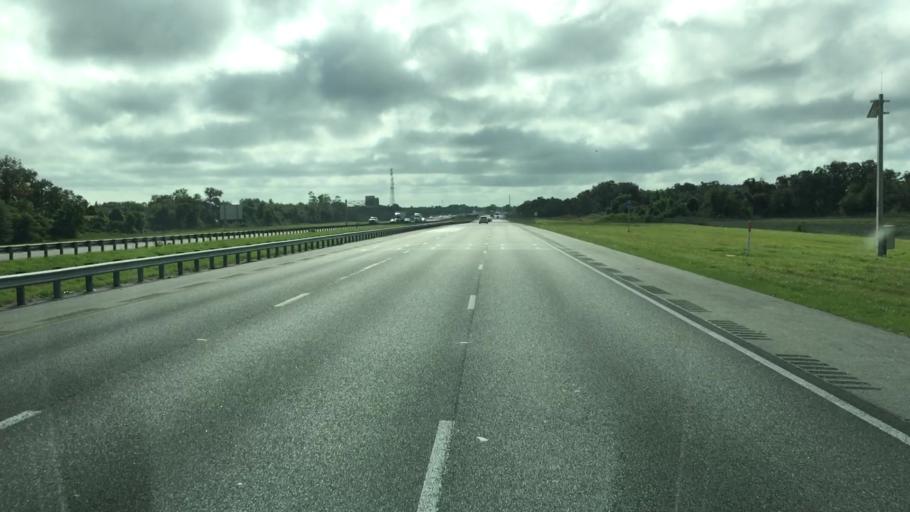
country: US
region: Florida
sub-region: Volusia County
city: Port Orange
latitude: 29.0970
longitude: -81.0244
